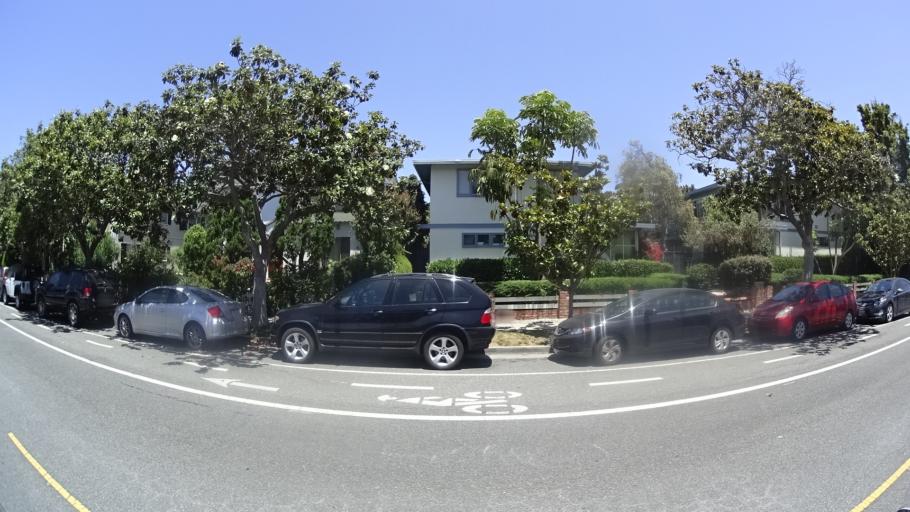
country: US
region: California
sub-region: Los Angeles County
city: Santa Monica
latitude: 34.0255
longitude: -118.5021
